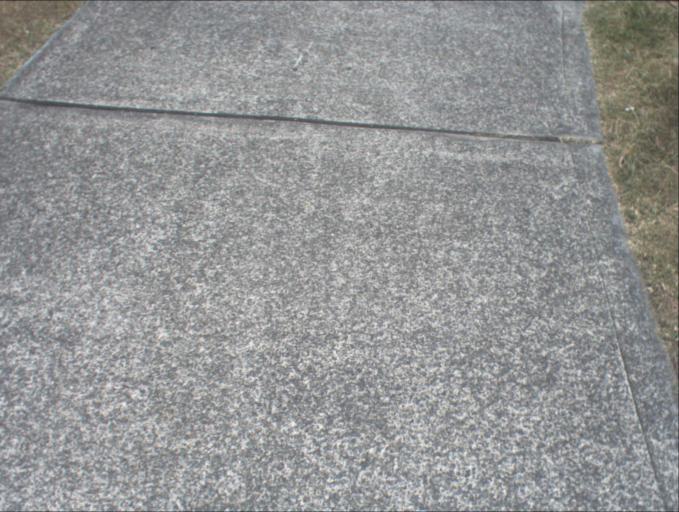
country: AU
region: Queensland
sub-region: Logan
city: Windaroo
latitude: -27.7422
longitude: 153.1928
